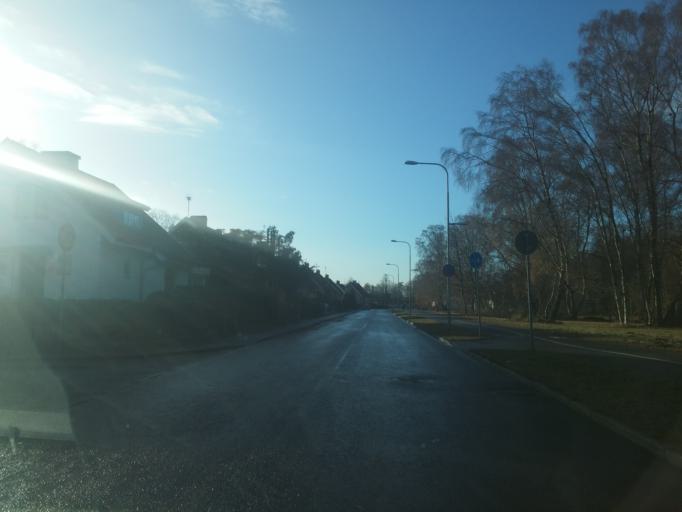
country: SE
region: Skane
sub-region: Angelholms Kommun
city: AEngelholm
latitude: 56.2361
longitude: 12.8466
